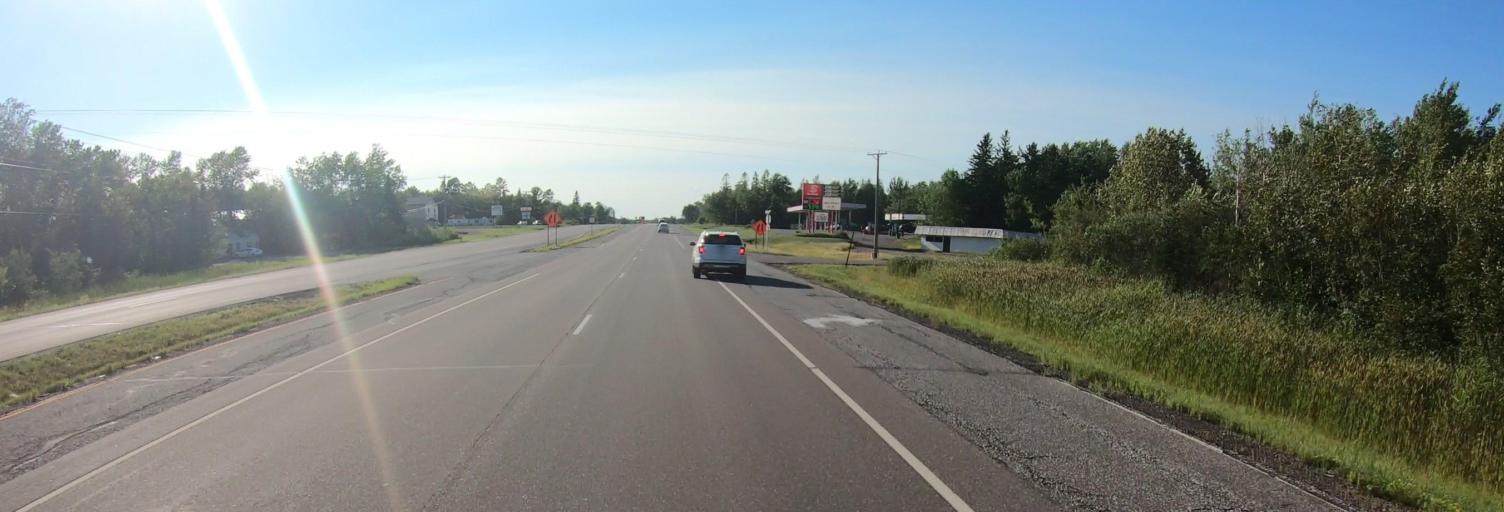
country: US
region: Minnesota
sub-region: Saint Louis County
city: Hermantown
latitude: 46.8474
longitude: -92.2693
